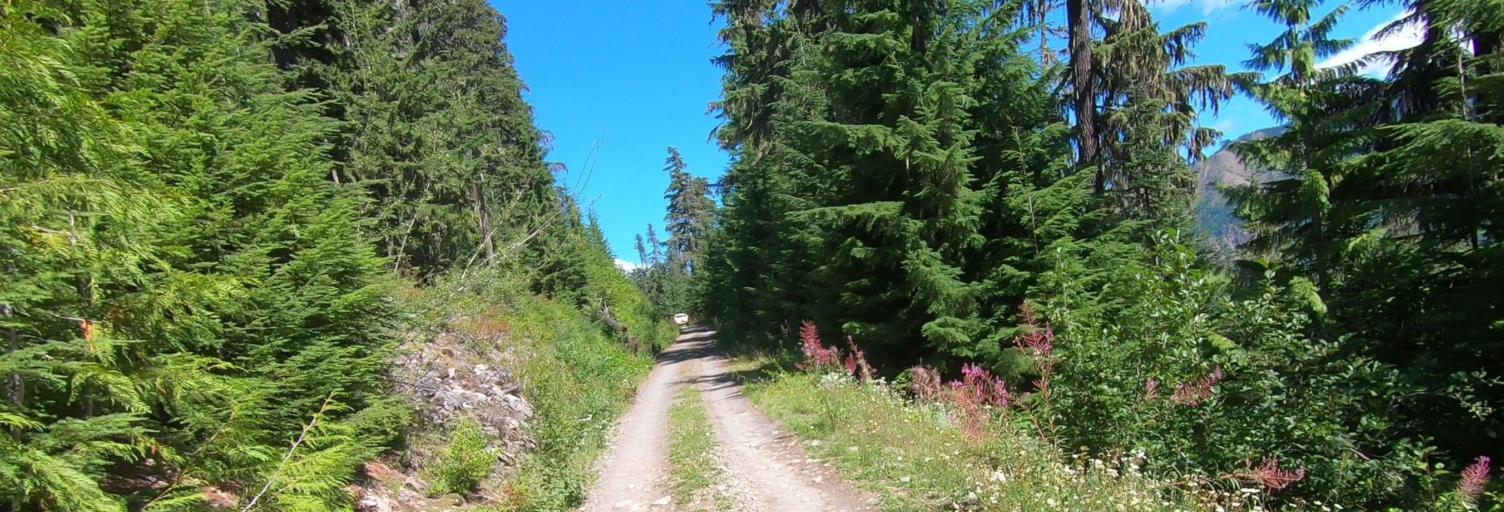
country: CA
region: British Columbia
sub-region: Fraser Valley Regional District
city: Chilliwack
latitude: 48.8556
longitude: -121.7949
